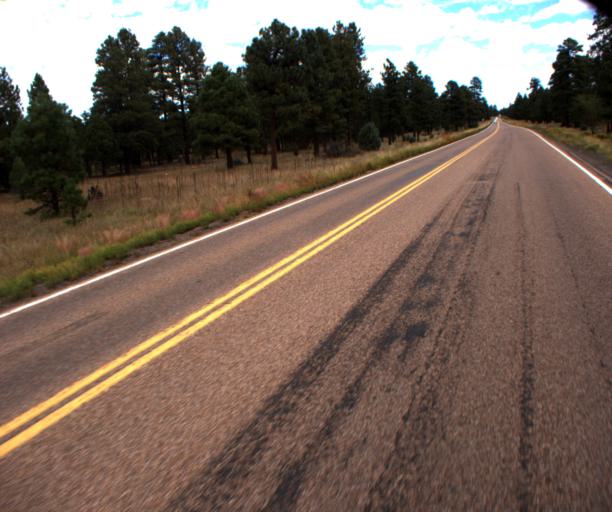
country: US
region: Arizona
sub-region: Navajo County
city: Heber-Overgaard
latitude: 34.4127
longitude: -110.6607
